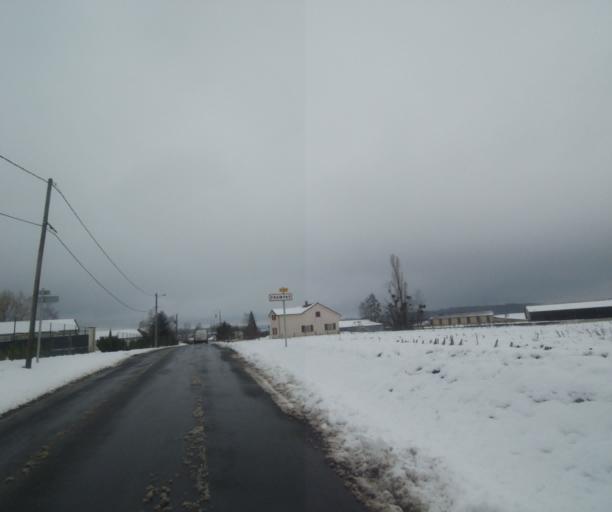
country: FR
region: Champagne-Ardenne
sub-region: Departement de la Haute-Marne
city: Montier-en-Der
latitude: 48.5184
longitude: 4.8102
